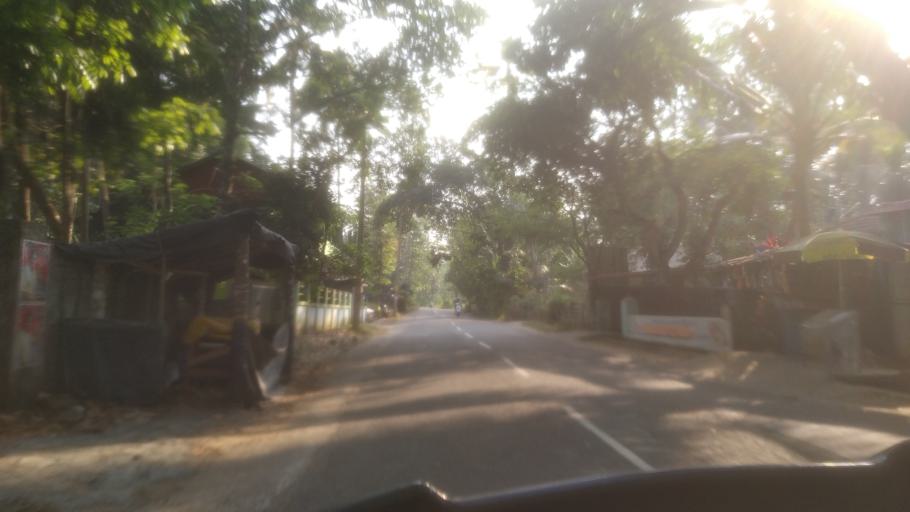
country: IN
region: Kerala
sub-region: Ernakulam
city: Piravam
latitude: 9.8182
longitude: 76.5012
